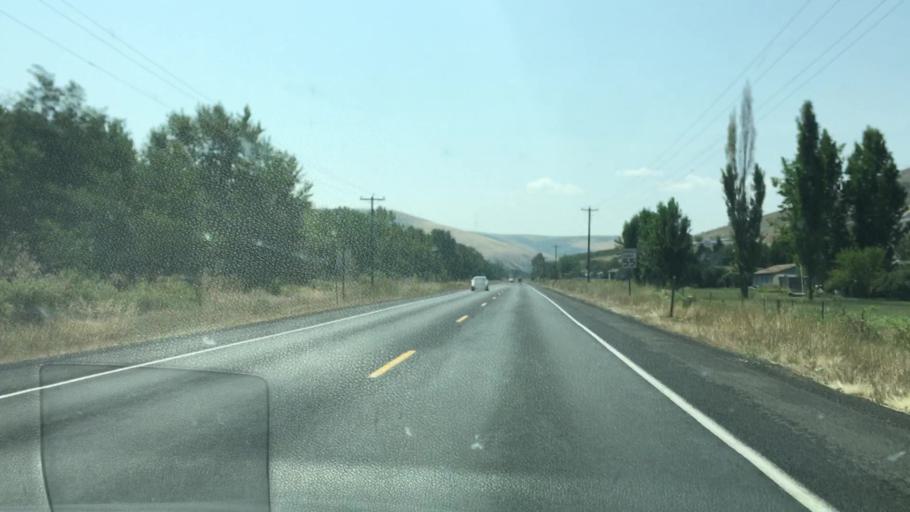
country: US
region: Idaho
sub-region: Nez Perce County
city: Lapwai
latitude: 46.3952
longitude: -116.7993
